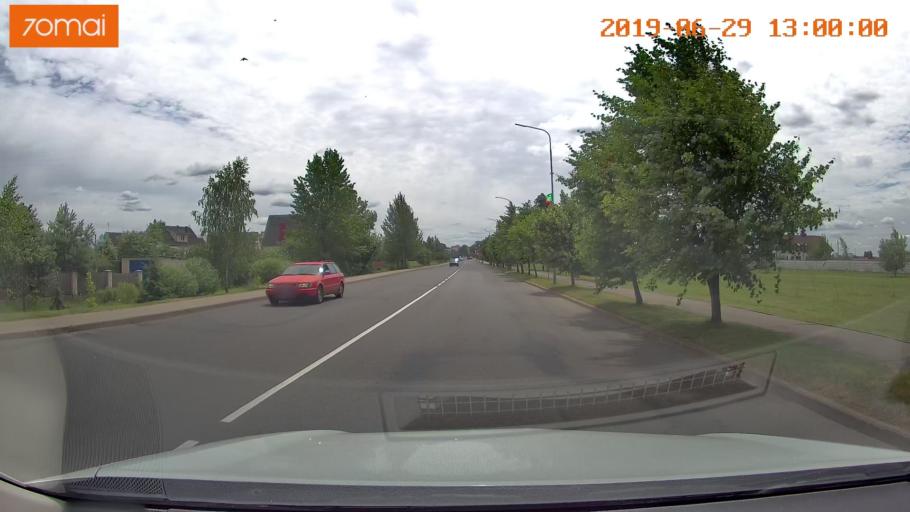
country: BY
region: Minsk
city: Slutsk
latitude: 53.0482
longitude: 27.5551
